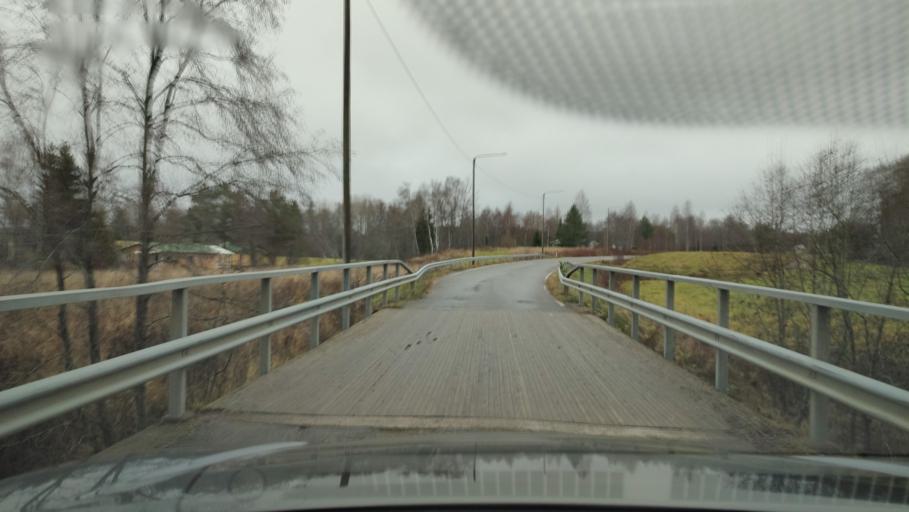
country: FI
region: Southern Ostrobothnia
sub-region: Suupohja
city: Isojoki
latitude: 62.1800
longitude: 21.9060
